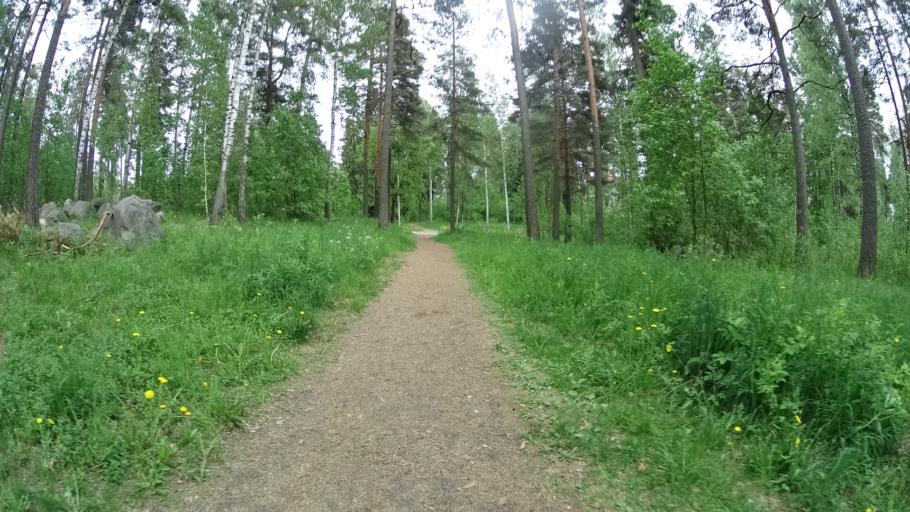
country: FI
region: Uusimaa
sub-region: Helsinki
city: Vantaa
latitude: 60.2959
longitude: 25.0535
